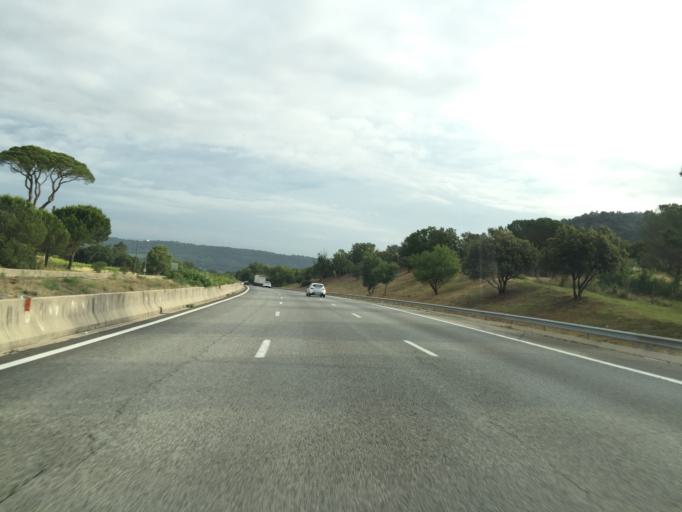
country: FR
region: Provence-Alpes-Cote d'Azur
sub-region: Departement du Var
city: Les Arcs
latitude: 43.4247
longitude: 6.4684
